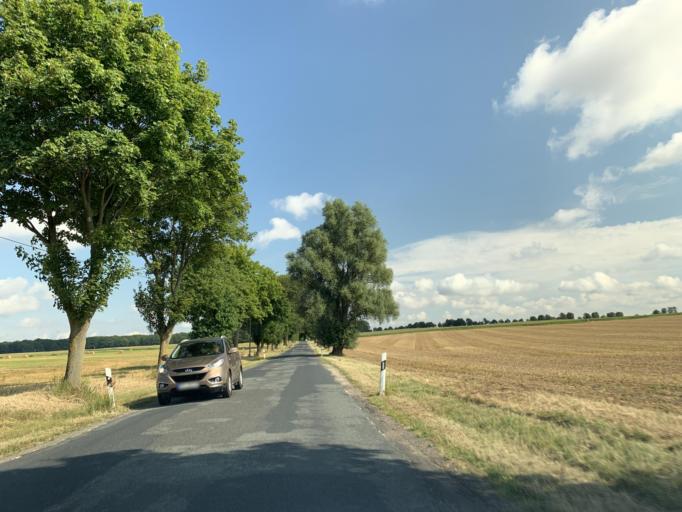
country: DE
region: Mecklenburg-Vorpommern
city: Loitz
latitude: 53.3630
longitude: 13.3587
